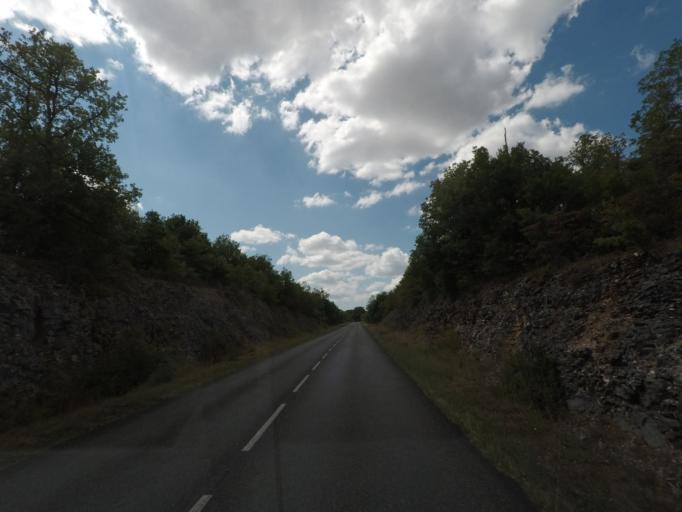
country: FR
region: Midi-Pyrenees
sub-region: Departement du Lot
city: Cajarc
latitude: 44.5699
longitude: 1.6749
